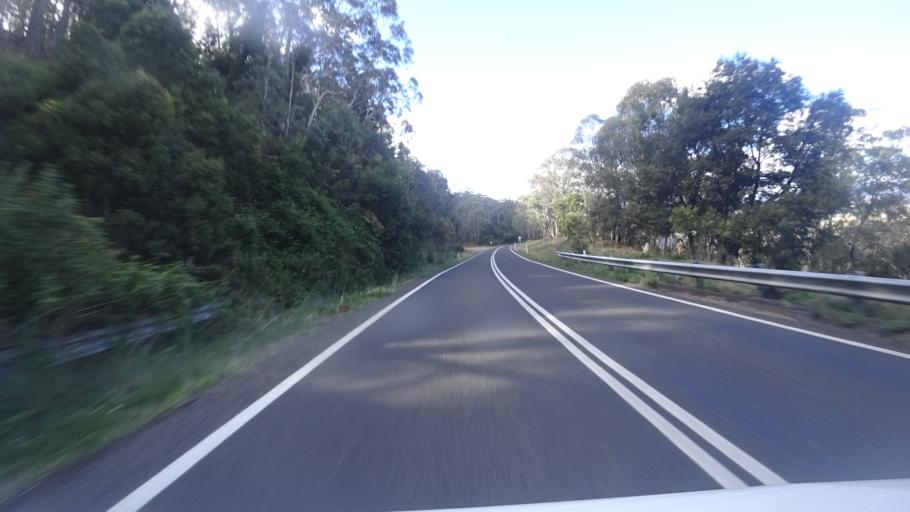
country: AU
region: New South Wales
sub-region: Lithgow
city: Bowenfels
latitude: -33.6665
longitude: 150.0486
